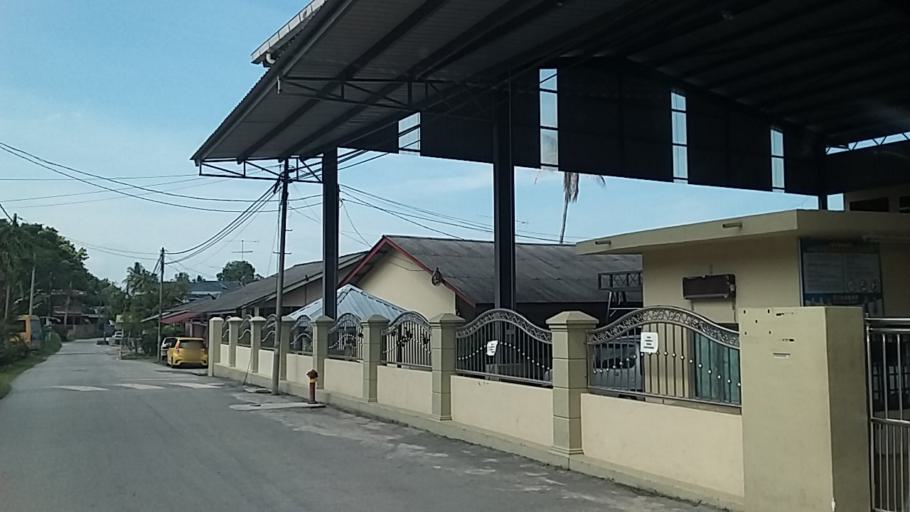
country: MY
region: Johor
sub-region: Daerah Batu Pahat
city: Batu Pahat
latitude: 1.7880
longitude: 102.8931
